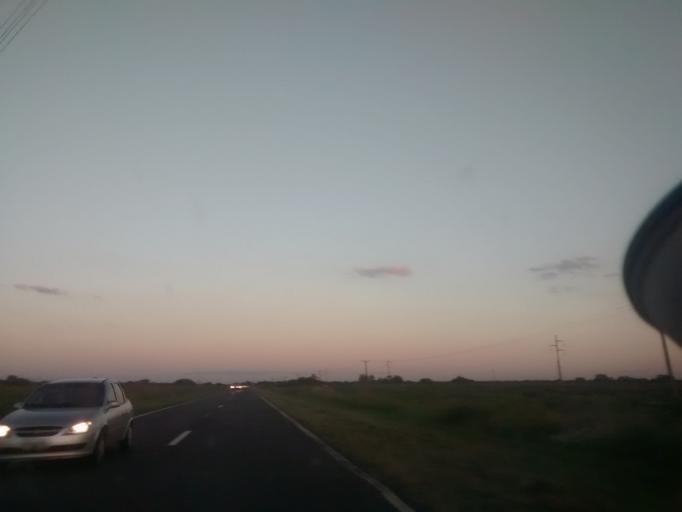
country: AR
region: Chaco
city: Lapachito
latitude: -27.1696
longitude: -59.3678
